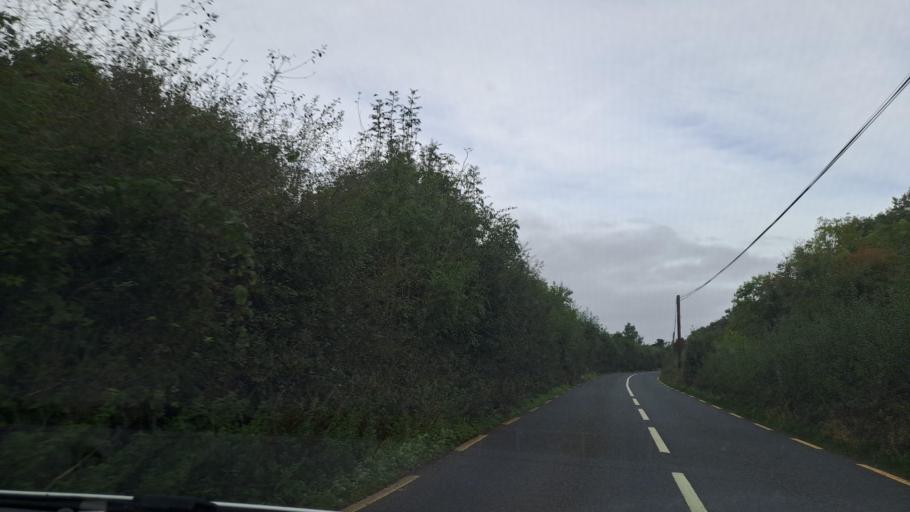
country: IE
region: Ulster
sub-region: County Monaghan
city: Carrickmacross
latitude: 53.8676
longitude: -6.6909
